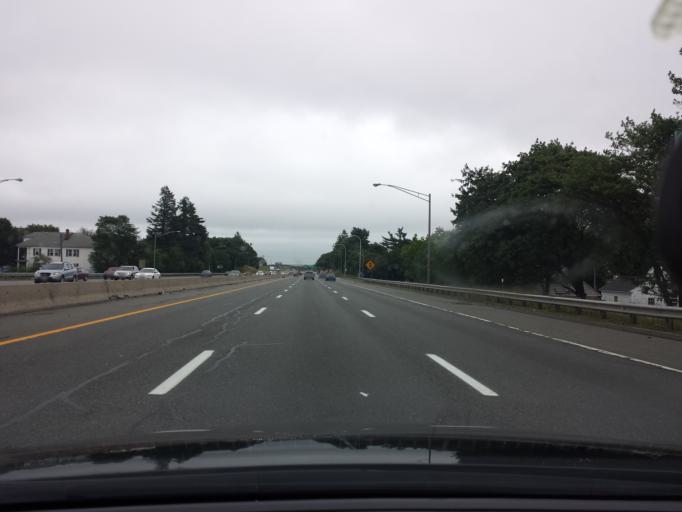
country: US
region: Rhode Island
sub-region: Providence County
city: East Providence
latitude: 41.8137
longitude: -71.3659
